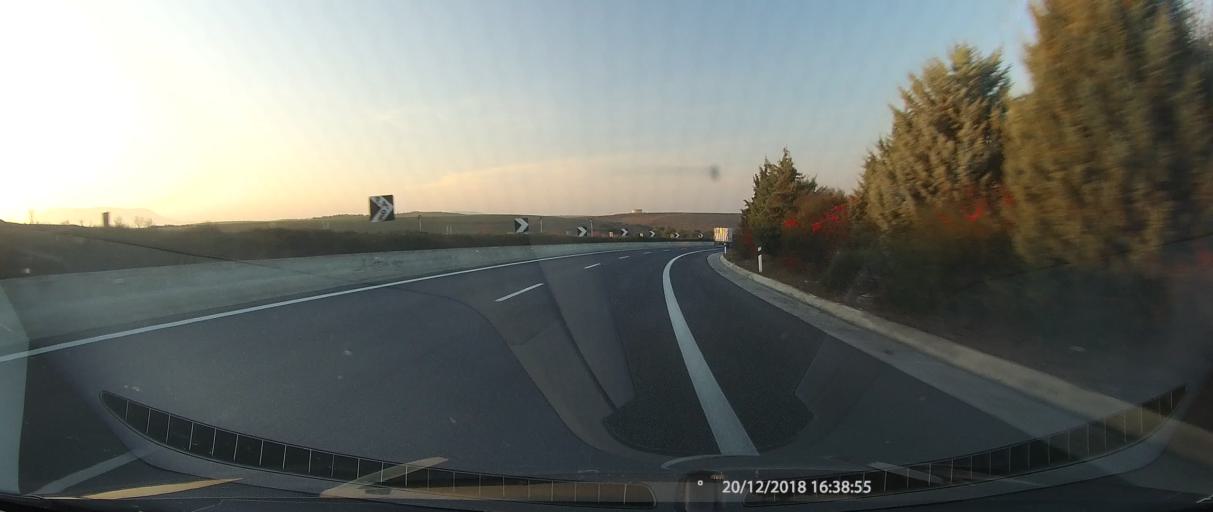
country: GR
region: Thessaly
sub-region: Nomos Magnisias
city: Velestino
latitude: 39.3490
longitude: 22.7737
